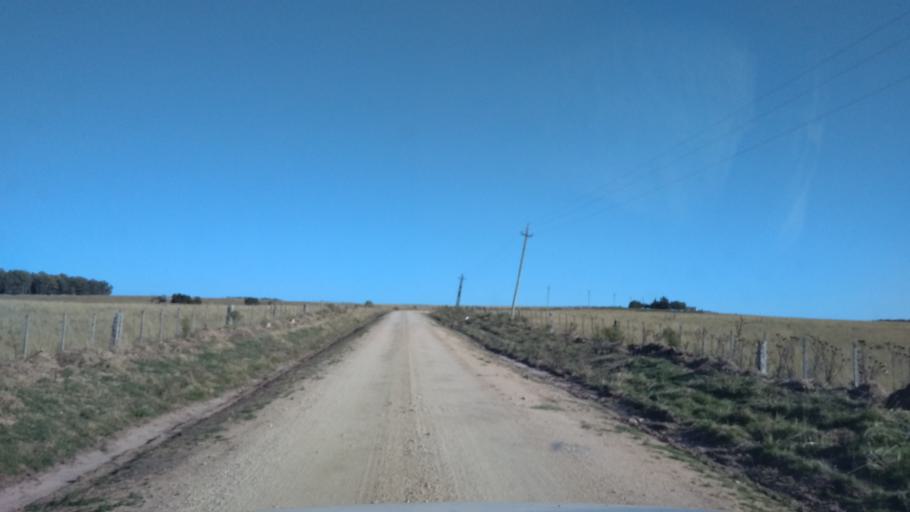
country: UY
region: Florida
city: Casupa
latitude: -34.0209
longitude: -55.7847
